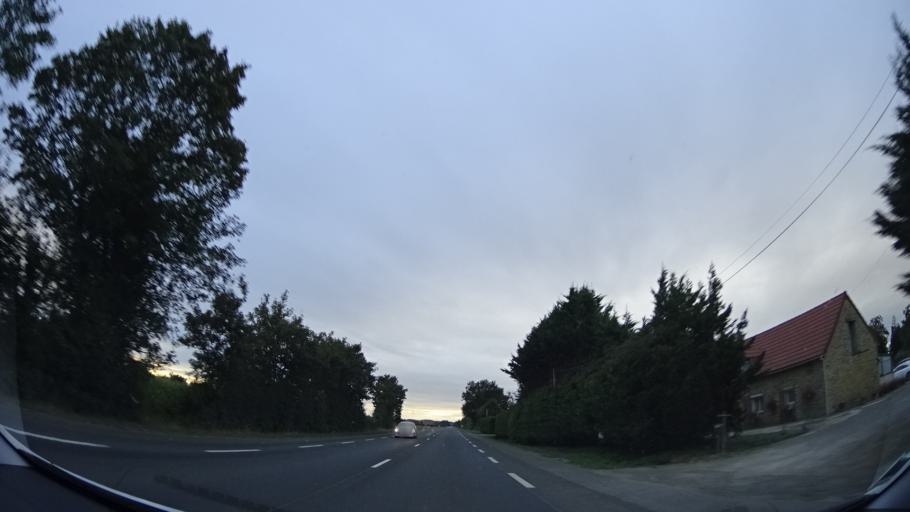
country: FR
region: Pays de la Loire
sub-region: Departement de la Sarthe
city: Coulans-sur-Gee
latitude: 48.0186
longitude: -0.0364
